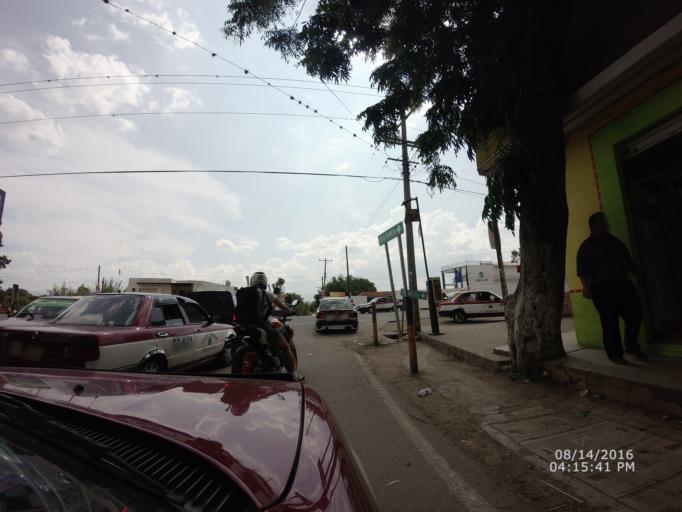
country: MX
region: Oaxaca
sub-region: San Lorenzo Cacaotepec
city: Santiago Etla
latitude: 17.1660
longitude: -96.7871
